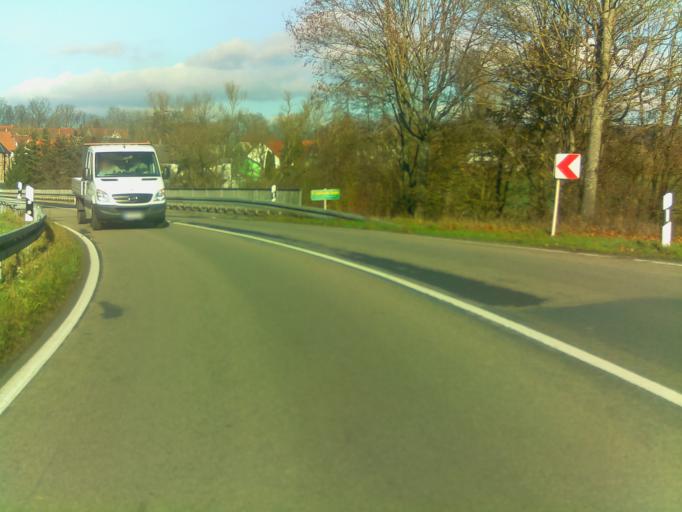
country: DE
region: Bavaria
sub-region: Regierungsbezirk Unterfranken
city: Bad Bocklet
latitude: 50.2350
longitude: 10.0745
